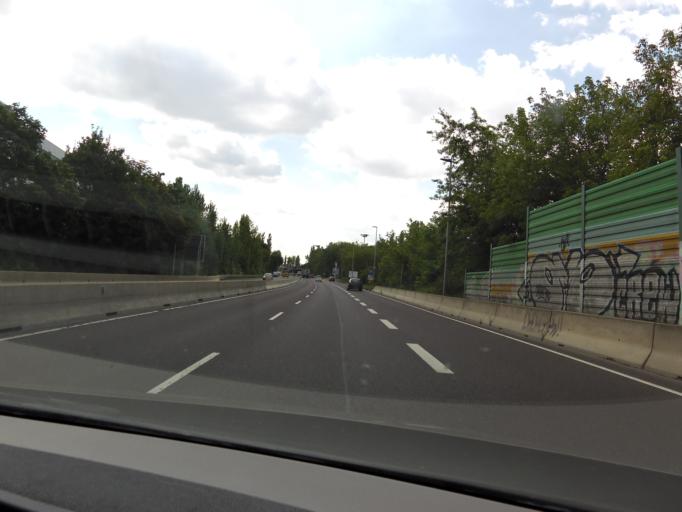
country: DE
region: Saxony-Anhalt
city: Neue Neustadt
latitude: 52.1633
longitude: 11.6271
